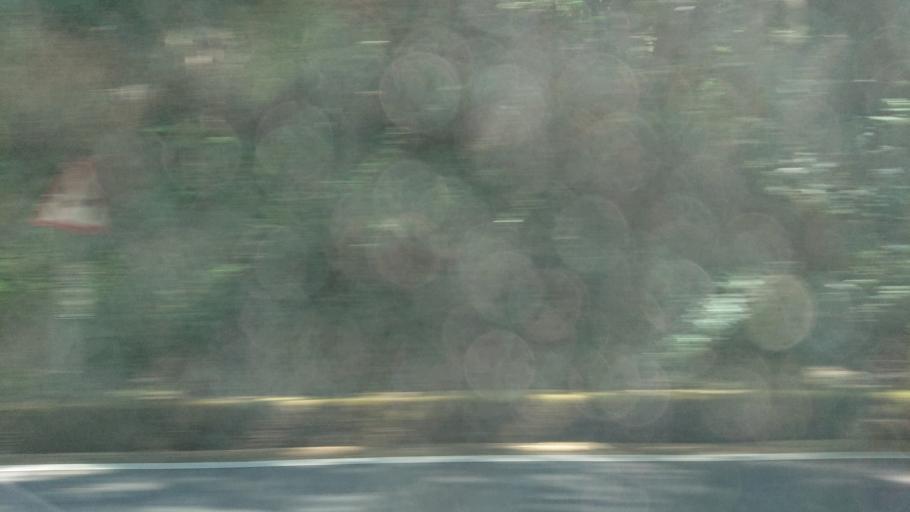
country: TW
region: Taiwan
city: Lugu
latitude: 23.4853
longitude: 120.8294
